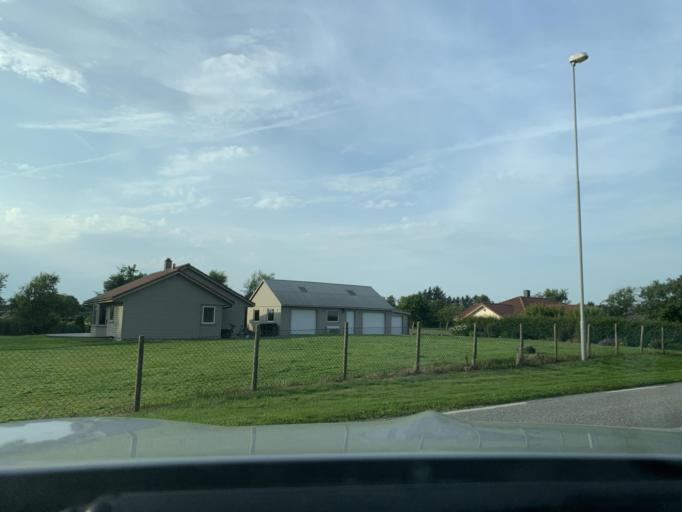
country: NO
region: Rogaland
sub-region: Time
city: Bryne
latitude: 58.7384
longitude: 5.6115
